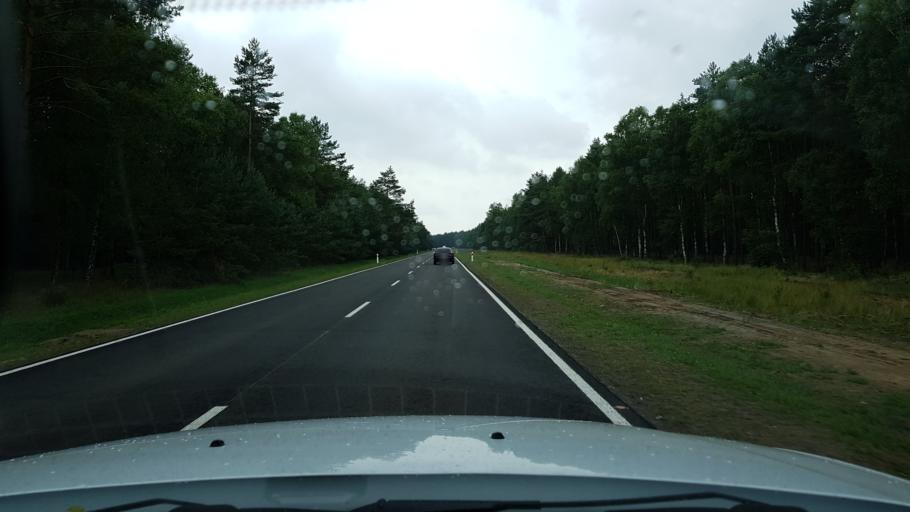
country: PL
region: West Pomeranian Voivodeship
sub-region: Powiat stargardzki
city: Kobylanka
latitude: 53.4361
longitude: 14.8680
